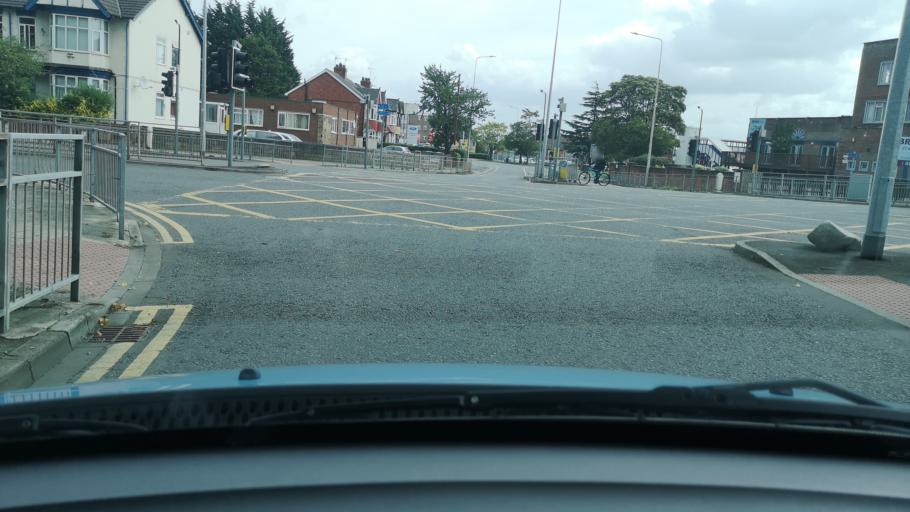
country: GB
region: England
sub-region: North Lincolnshire
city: Scunthorpe
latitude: 53.5863
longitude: -0.6544
